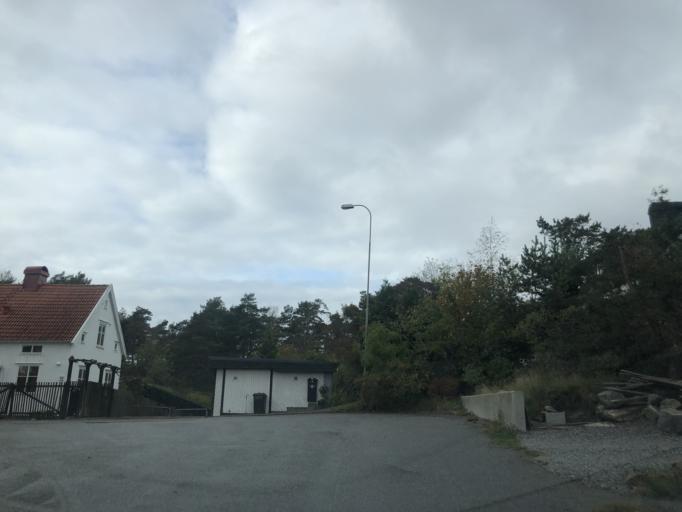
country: SE
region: Vaestra Goetaland
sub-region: Goteborg
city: Majorna
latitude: 57.6729
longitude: 11.9022
